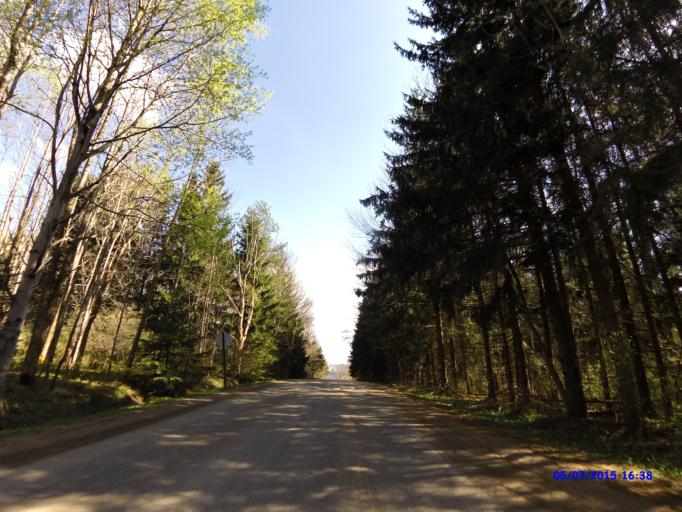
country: US
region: New York
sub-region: Cattaraugus County
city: Little Valley
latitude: 42.3112
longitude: -78.6814
